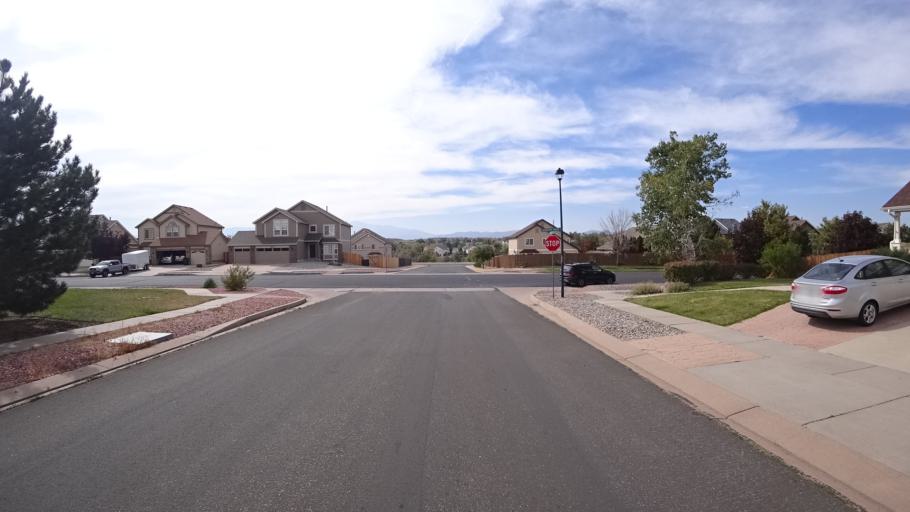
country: US
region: Colorado
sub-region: El Paso County
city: Cimarron Hills
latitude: 38.9104
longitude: -104.7000
